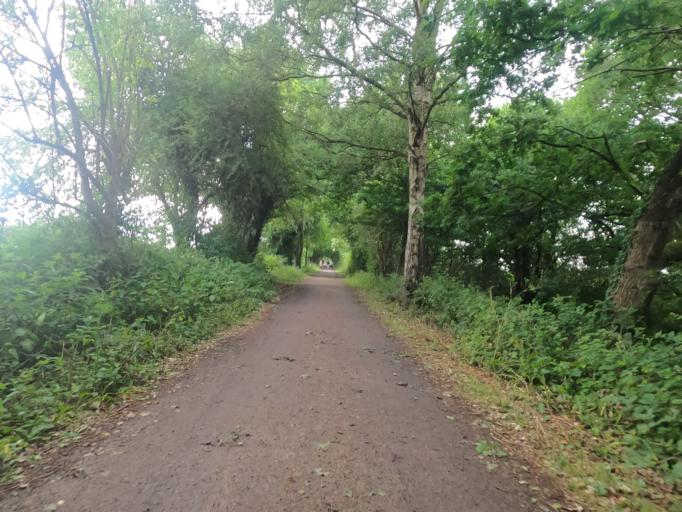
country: GB
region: England
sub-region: Cheshire West and Chester
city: Winsford
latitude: 53.2054
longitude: -2.5276
